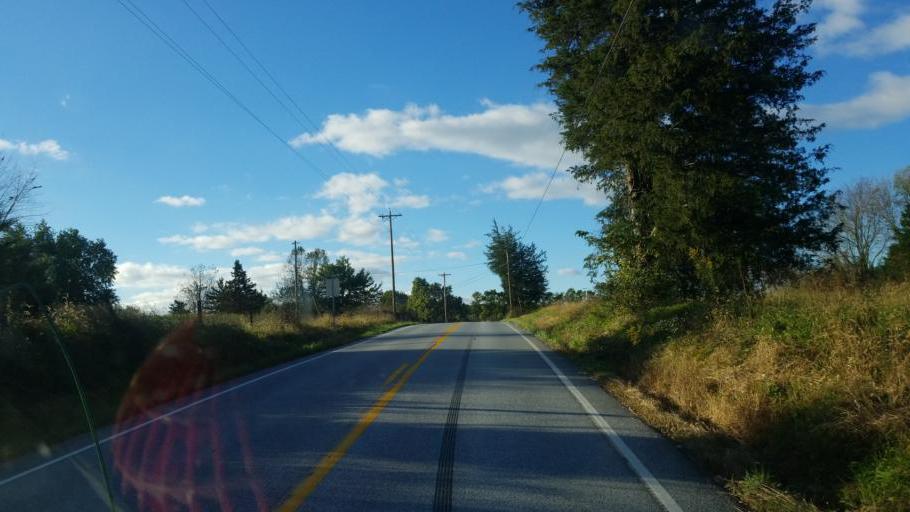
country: US
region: Pennsylvania
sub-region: Adams County
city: Gettysburg
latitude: 39.8752
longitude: -77.2307
